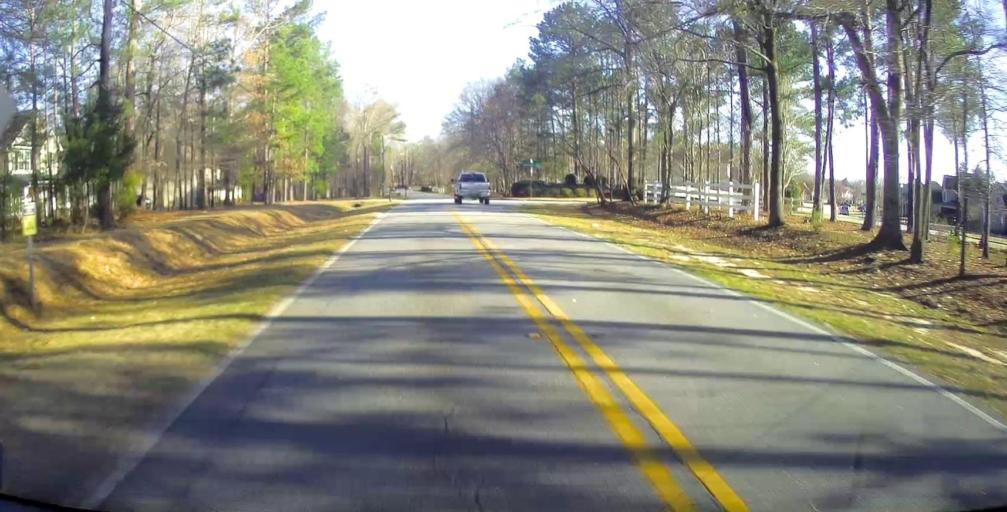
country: US
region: Georgia
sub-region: Harris County
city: Hamilton
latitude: 32.5679
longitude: -84.8024
